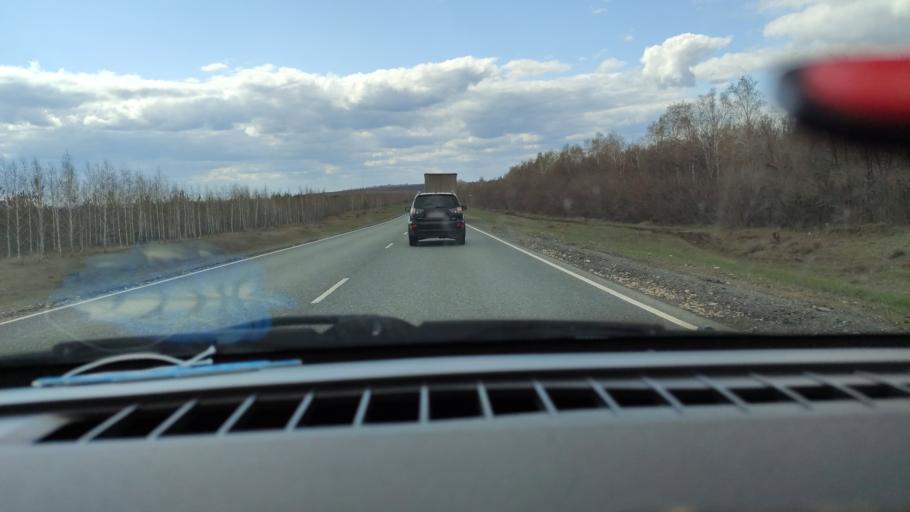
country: RU
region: Saratov
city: Balakovo
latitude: 52.1471
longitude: 47.8075
